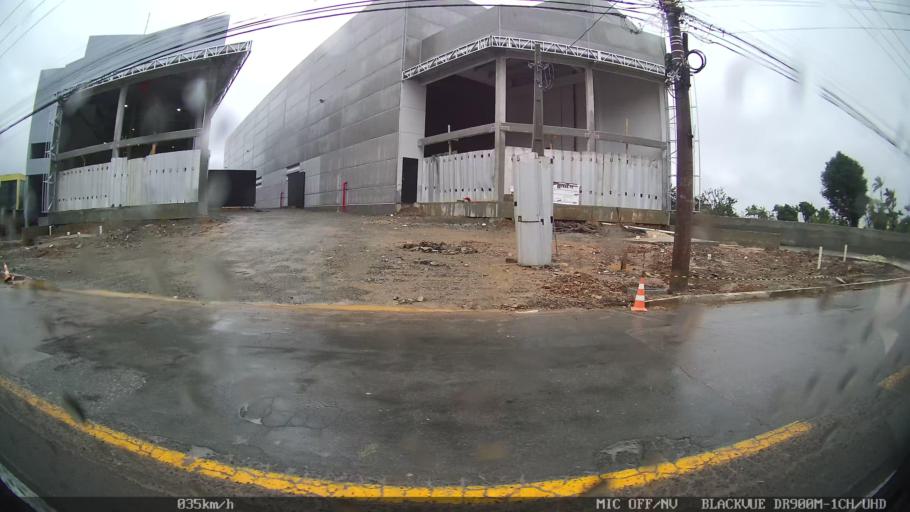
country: BR
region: Santa Catarina
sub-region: Itajai
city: Itajai
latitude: -26.9279
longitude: -48.6842
